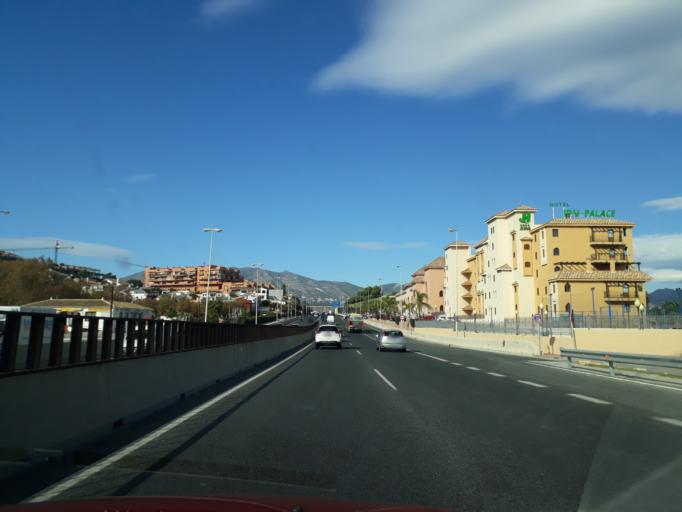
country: ES
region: Andalusia
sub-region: Provincia de Malaga
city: Fuengirola
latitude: 36.5201
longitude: -4.6301
